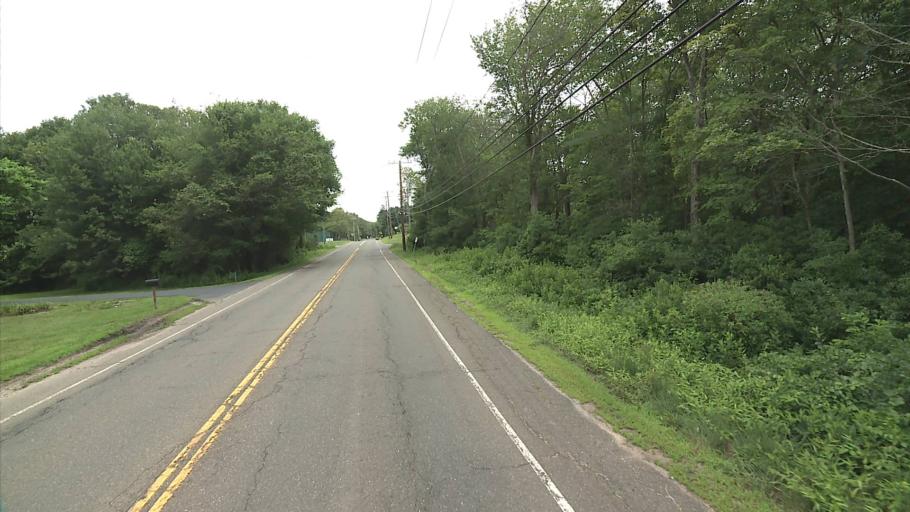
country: US
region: Connecticut
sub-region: Middlesex County
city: Clinton
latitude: 41.3574
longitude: -72.5529
